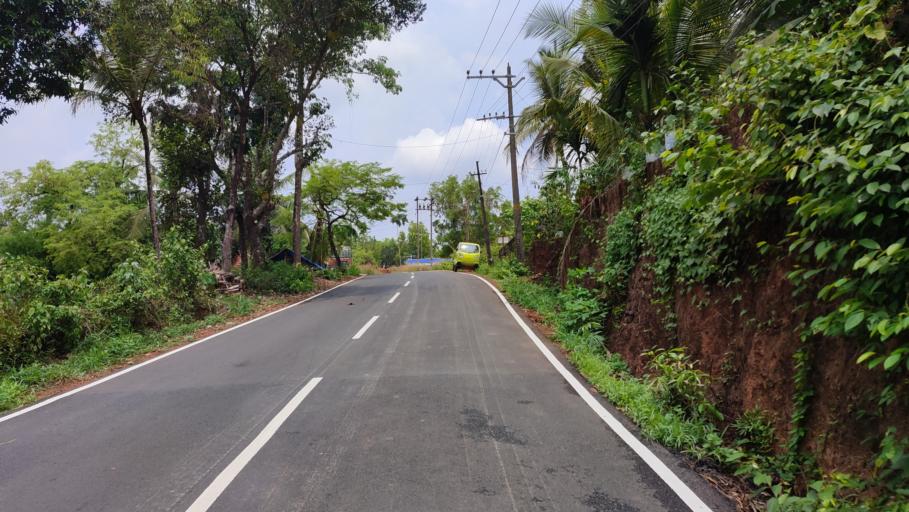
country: IN
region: Kerala
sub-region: Kasaragod District
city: Kannangad
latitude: 12.3154
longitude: 75.1381
